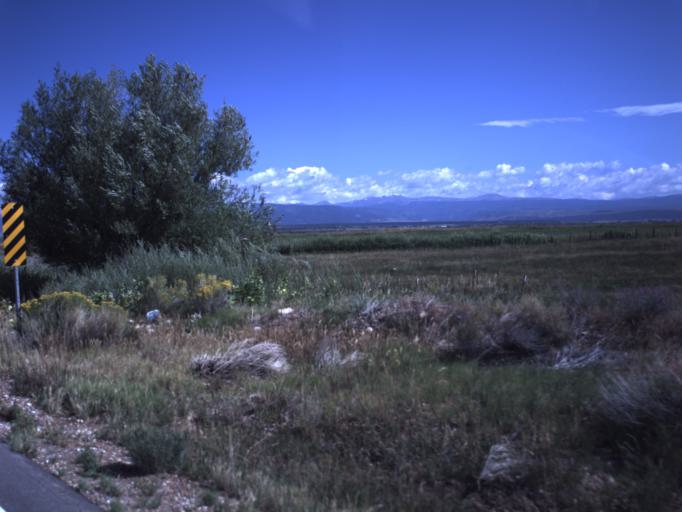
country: US
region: Utah
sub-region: Duchesne County
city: Duchesne
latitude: 40.3266
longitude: -110.4075
